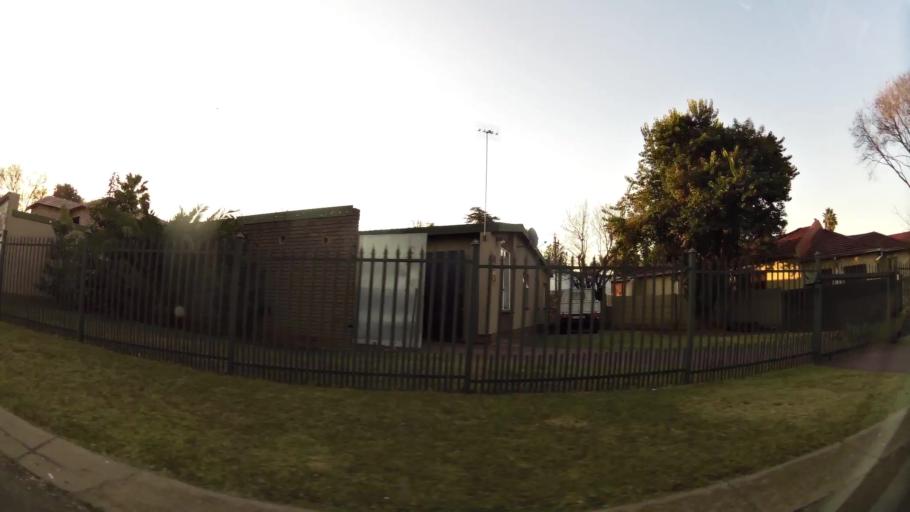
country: ZA
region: Gauteng
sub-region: City of Tshwane Metropolitan Municipality
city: Pretoria
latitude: -25.7460
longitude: 28.1196
